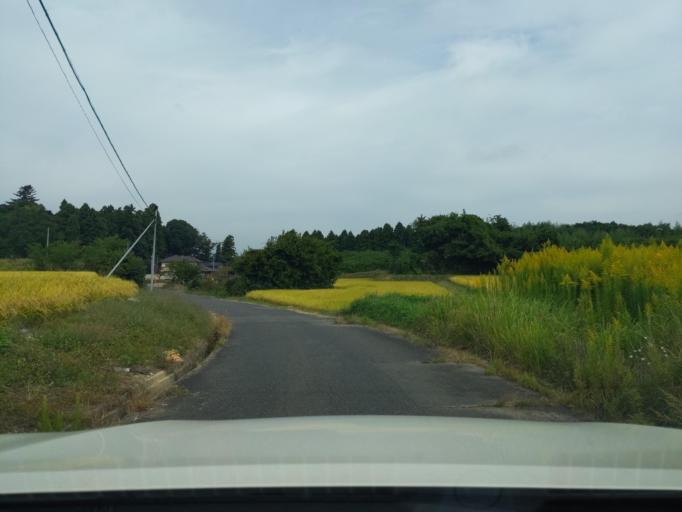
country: JP
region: Fukushima
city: Koriyama
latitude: 37.4120
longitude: 140.3232
